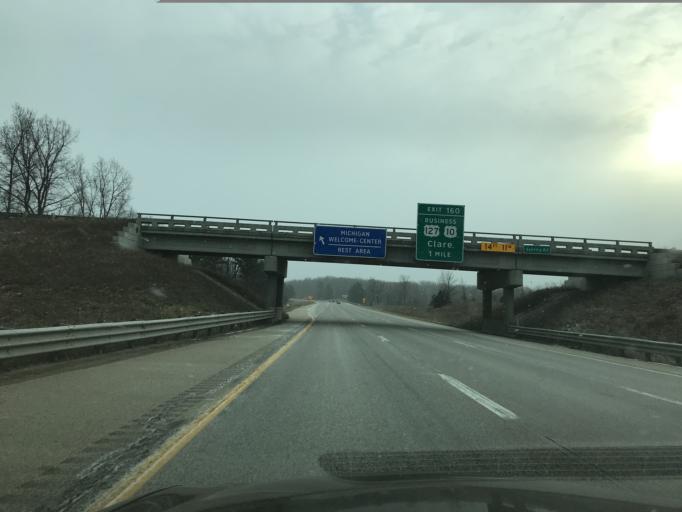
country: US
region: Michigan
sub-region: Clare County
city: Clare
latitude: 43.8571
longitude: -84.7789
